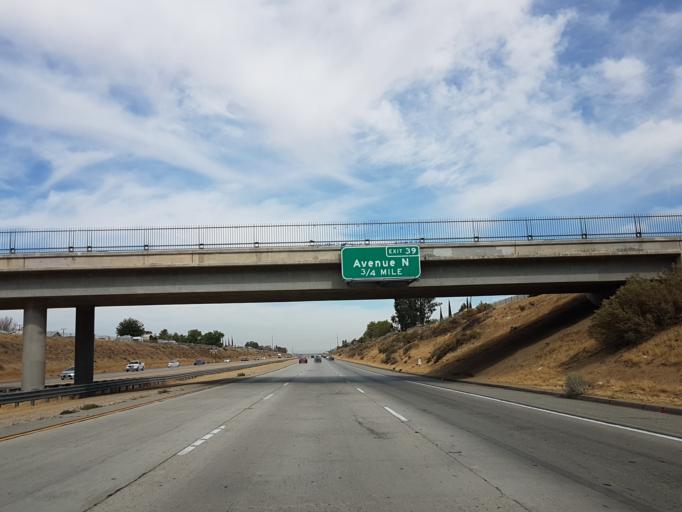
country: US
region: California
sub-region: Los Angeles County
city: Desert View Highlands
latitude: 34.6159
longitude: -118.1531
